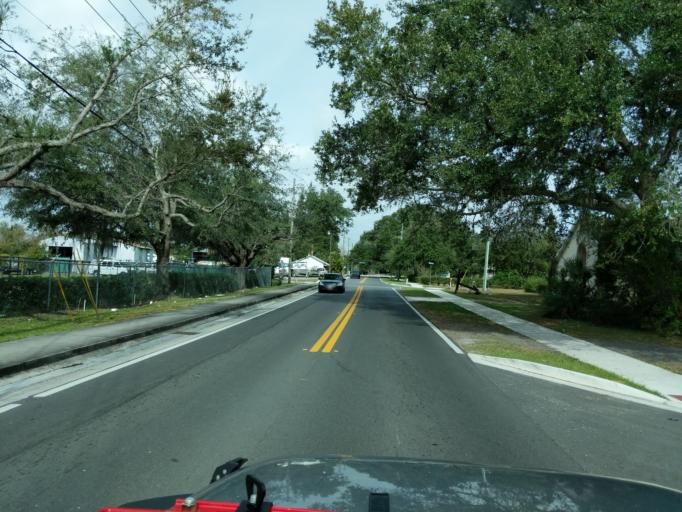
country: US
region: Florida
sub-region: Orange County
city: Winter Garden
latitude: 28.5651
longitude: -81.5753
